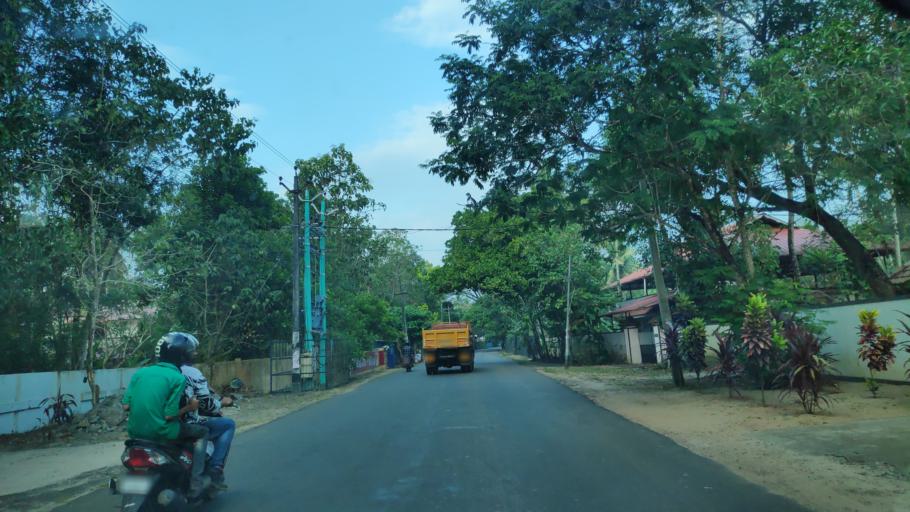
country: IN
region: Kerala
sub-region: Alappuzha
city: Shertallai
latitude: 9.6579
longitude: 76.3767
